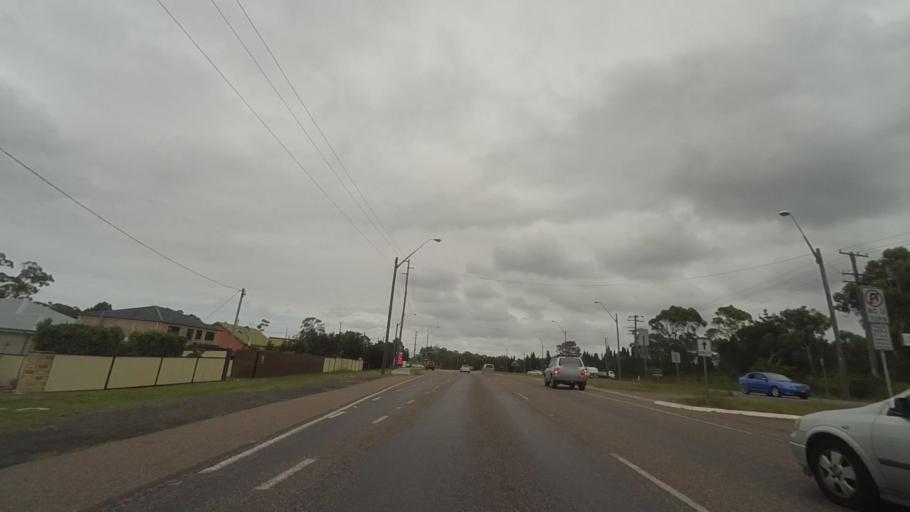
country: AU
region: New South Wales
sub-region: Wyong Shire
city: Buff Point
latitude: -33.1985
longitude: 151.5237
